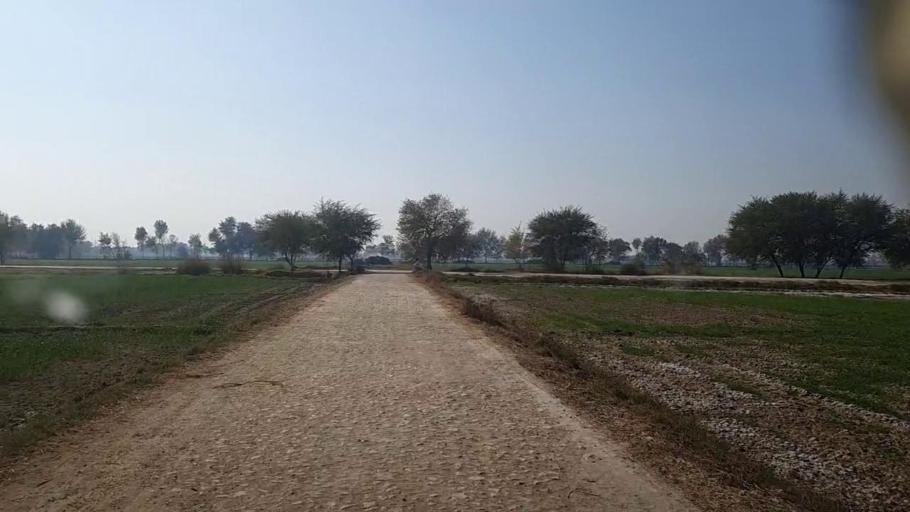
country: PK
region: Sindh
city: Khairpur
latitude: 27.9661
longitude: 69.7134
